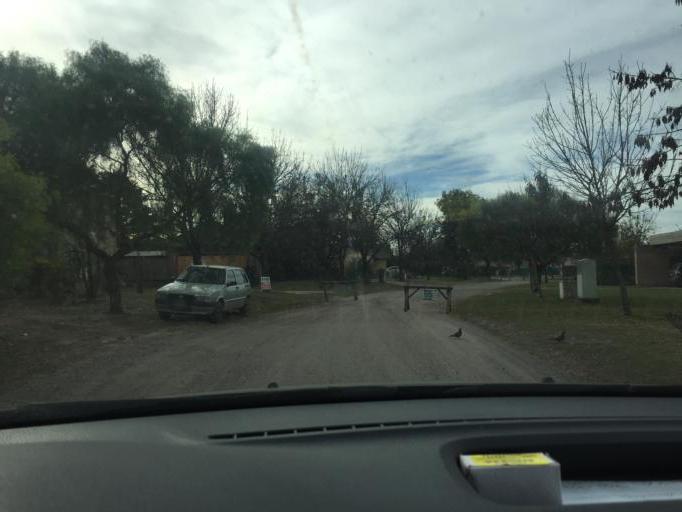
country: AR
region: Cordoba
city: Villa Allende
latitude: -31.3016
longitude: -64.2375
